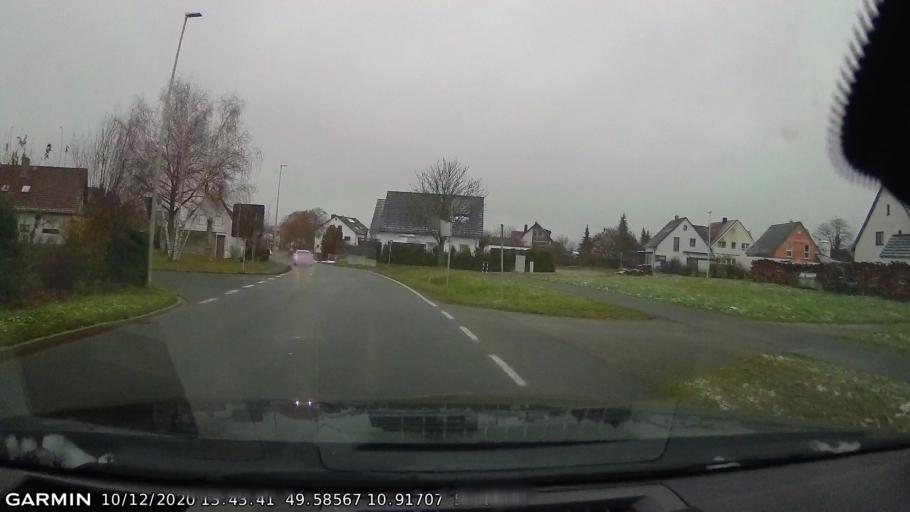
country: DE
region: Bavaria
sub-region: Regierungsbezirk Mittelfranken
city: Herzogenaurach
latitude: 49.5857
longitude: 10.9171
